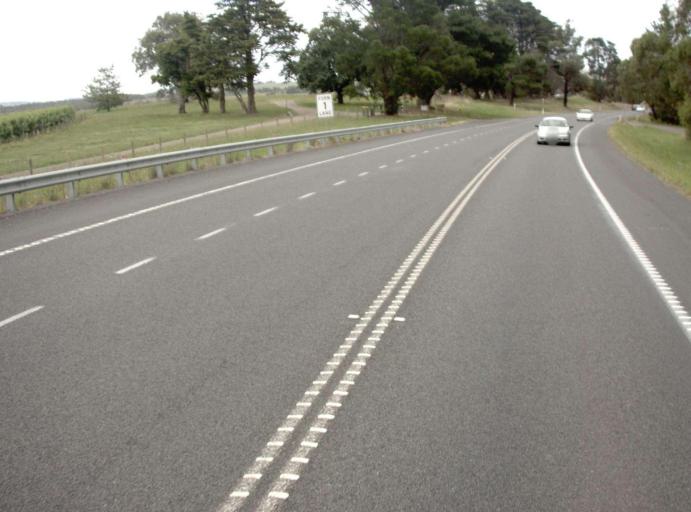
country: AU
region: Victoria
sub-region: Yarra Ranges
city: Badger Creek
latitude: -37.6847
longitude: 145.4819
